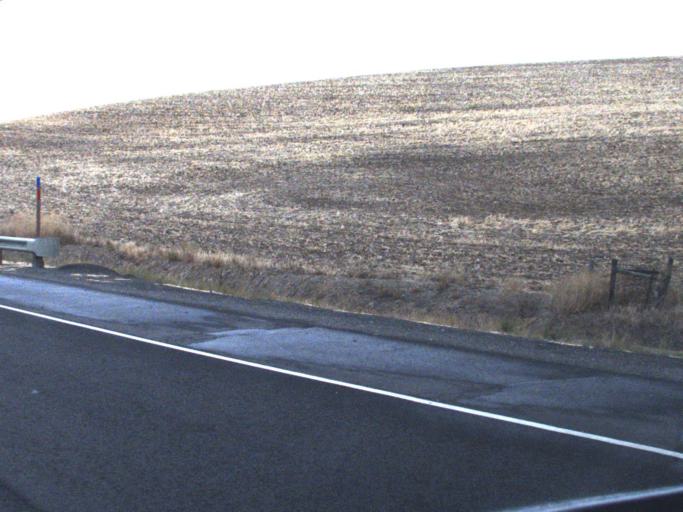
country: US
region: Washington
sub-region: Whitman County
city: Pullman
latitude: 46.7403
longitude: -117.2301
